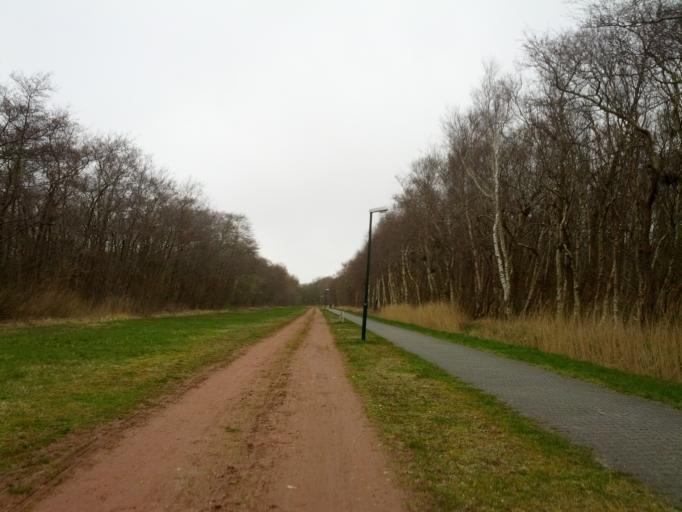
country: DE
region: Lower Saxony
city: Langeoog
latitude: 53.7339
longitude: 7.4830
